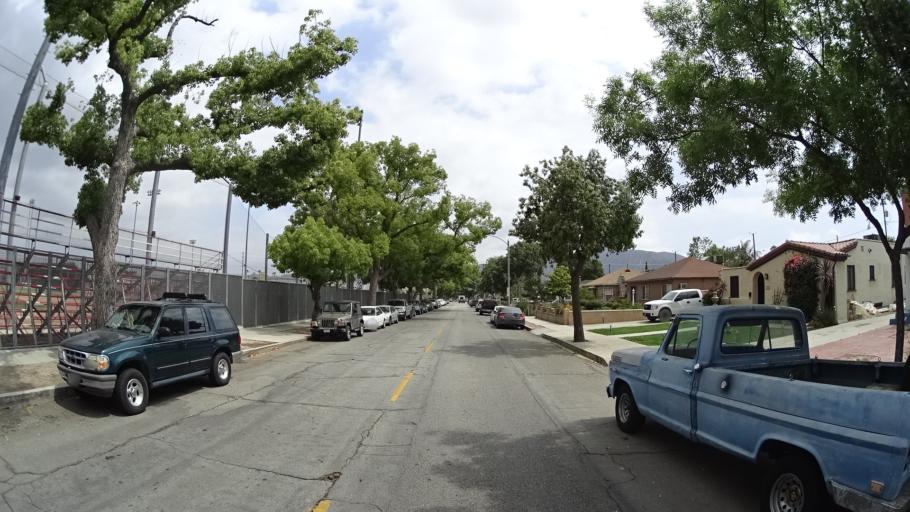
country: US
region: California
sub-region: Los Angeles County
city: Burbank
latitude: 34.1682
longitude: -118.3281
